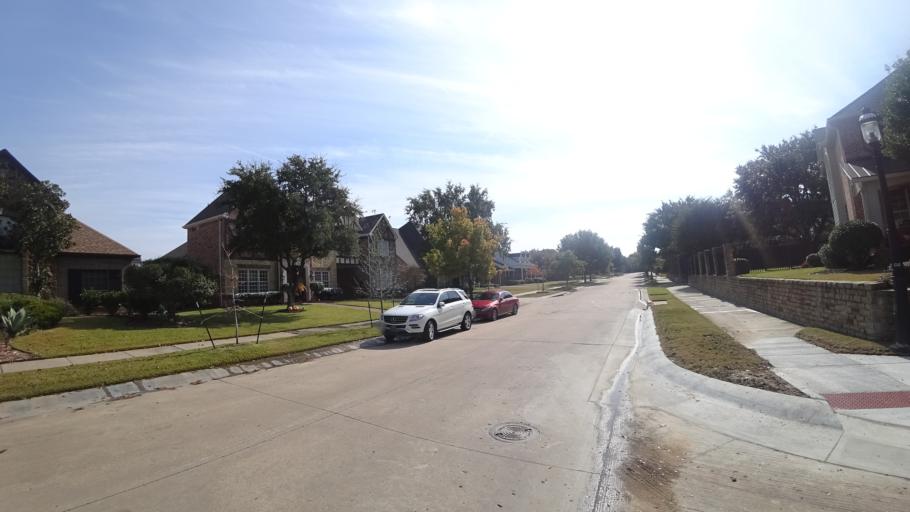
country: US
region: Texas
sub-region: Denton County
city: The Colony
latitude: 33.0347
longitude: -96.8889
